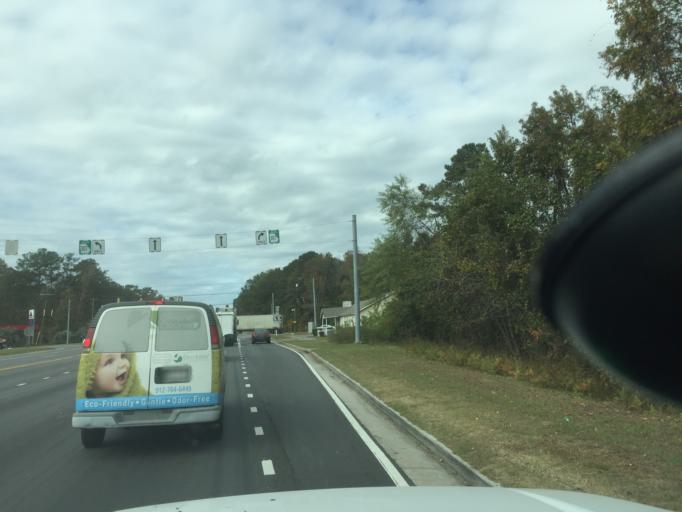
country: US
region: Georgia
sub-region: Chatham County
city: Garden City
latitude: 32.0925
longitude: -81.1956
